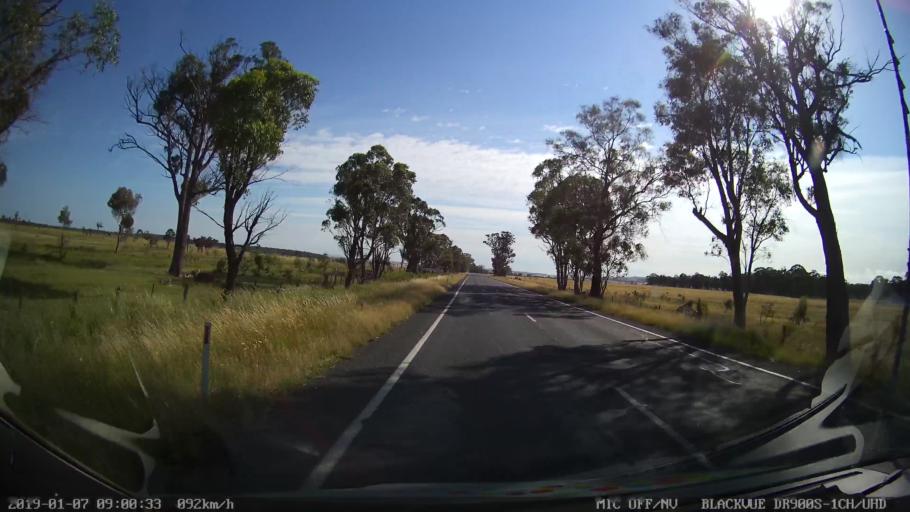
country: AU
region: New South Wales
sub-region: Armidale Dumaresq
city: Armidale
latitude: -30.7470
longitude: 151.3943
